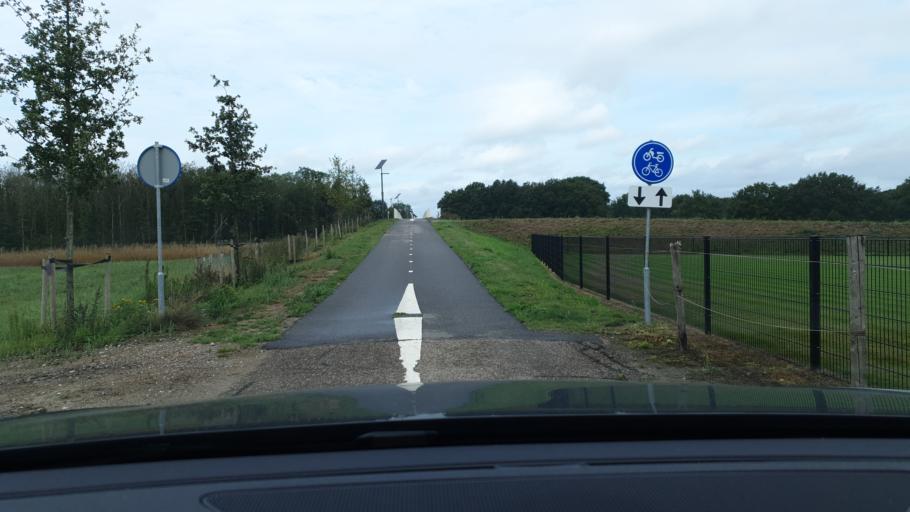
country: NL
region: Limburg
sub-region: Gemeente Bergen
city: Wellerlooi
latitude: 51.5366
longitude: 6.0652
